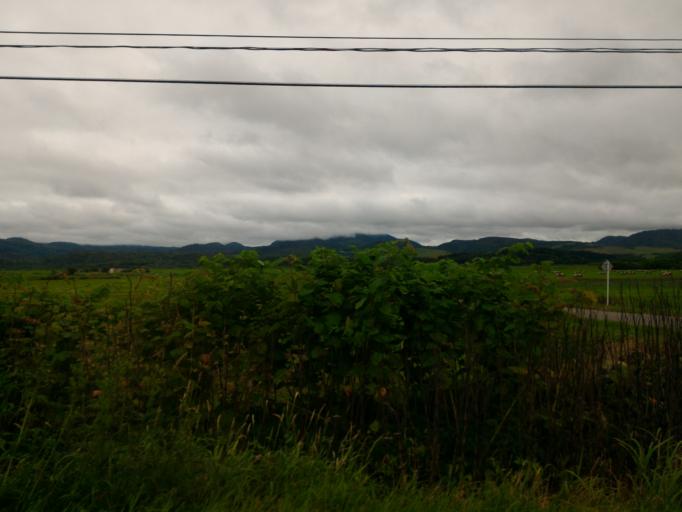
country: JP
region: Hokkaido
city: Makubetsu
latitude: 44.8286
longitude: 142.0614
